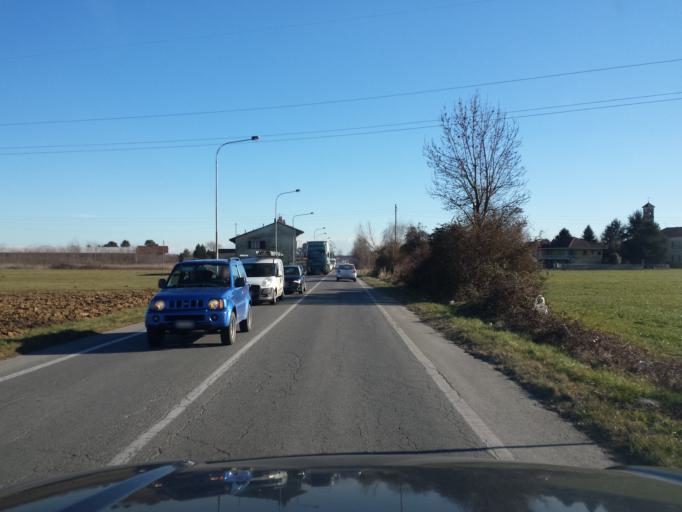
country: IT
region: Piedmont
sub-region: Provincia di Torino
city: Castellamonte
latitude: 45.3708
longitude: 7.7162
